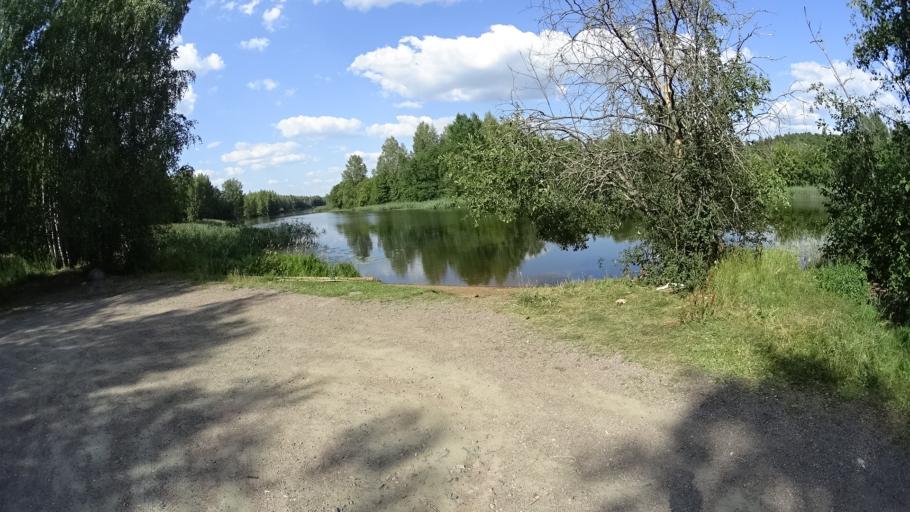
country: FI
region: Uusimaa
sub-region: Porvoo
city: Porvoo
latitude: 60.3983
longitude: 25.6441
